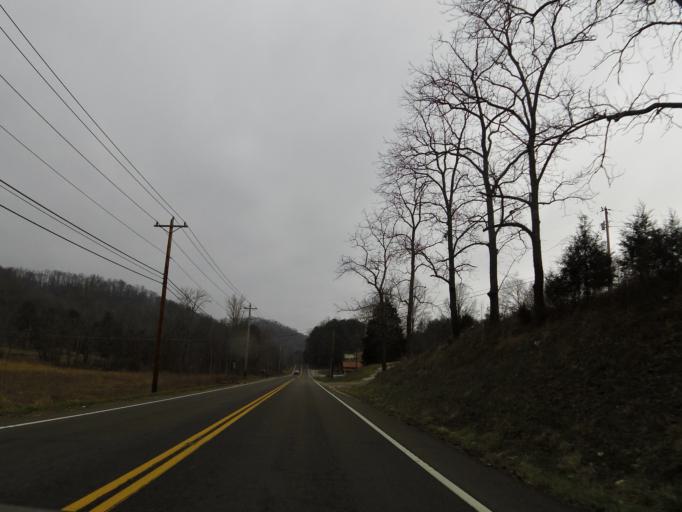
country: US
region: Tennessee
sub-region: Anderson County
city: Clinton
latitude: 36.1573
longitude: -84.1464
